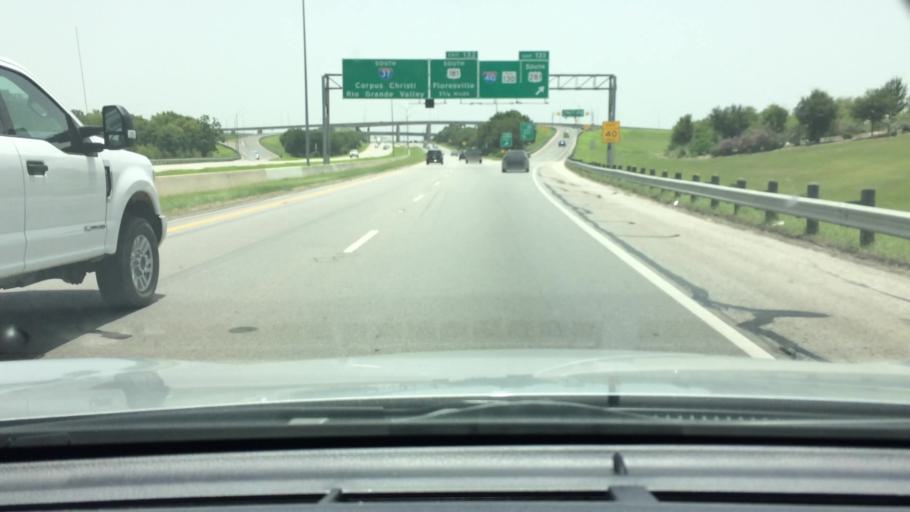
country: US
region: Texas
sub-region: Bexar County
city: China Grove
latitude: 29.3340
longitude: -98.4187
